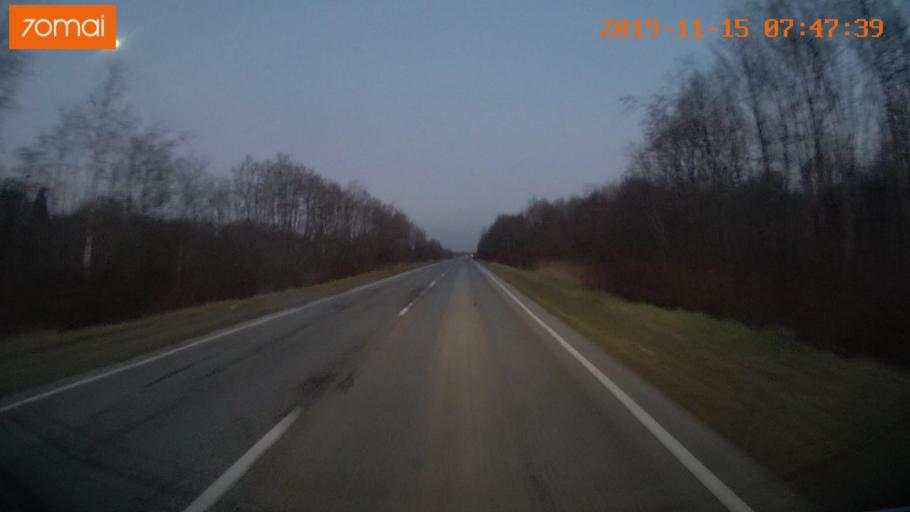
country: RU
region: Vologda
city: Sheksna
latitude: 58.8432
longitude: 38.2577
